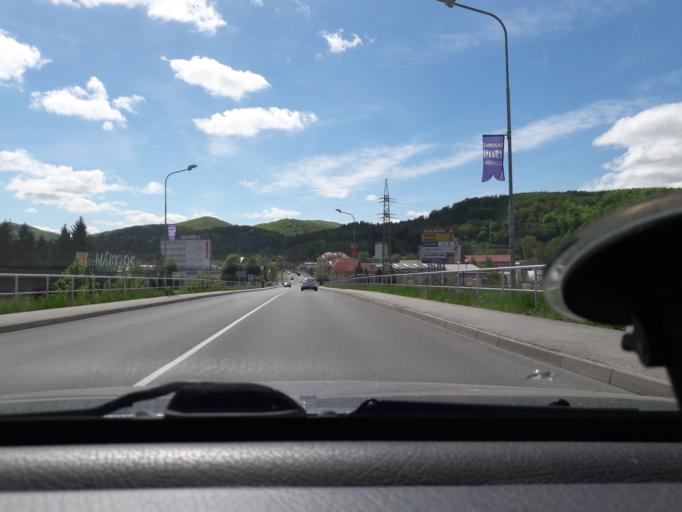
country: SK
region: Banskobystricky
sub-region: Okres Banska Bystrica
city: Zvolen
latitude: 48.5715
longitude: 19.1270
